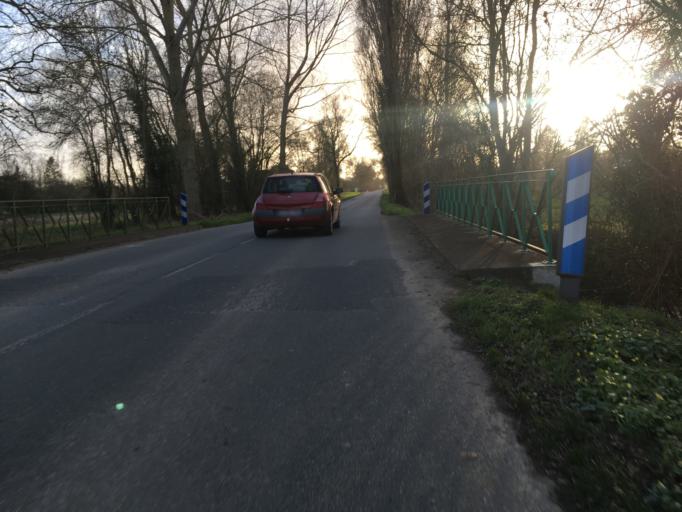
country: FR
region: Poitou-Charentes
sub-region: Departement de la Charente-Maritime
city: Courcon
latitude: 46.1689
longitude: -0.8504
